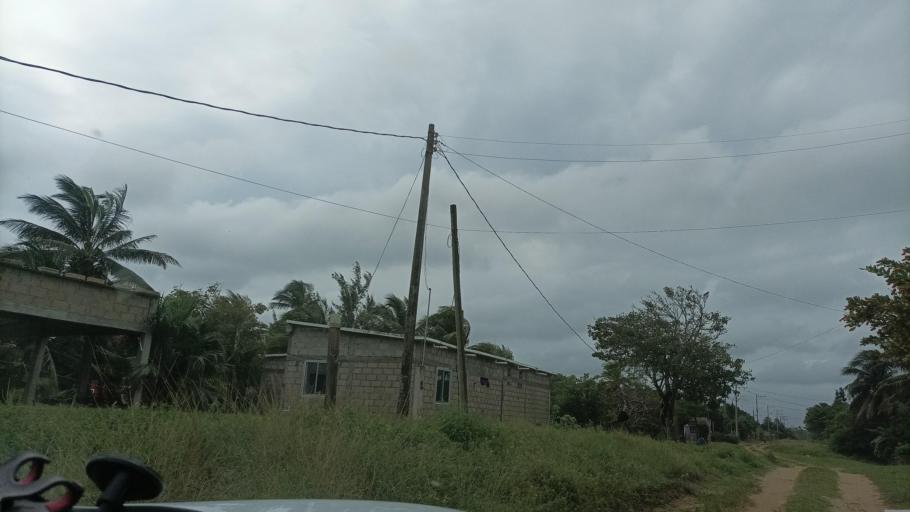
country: MX
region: Veracruz
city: Agua Dulce
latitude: 18.2079
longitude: -94.1434
